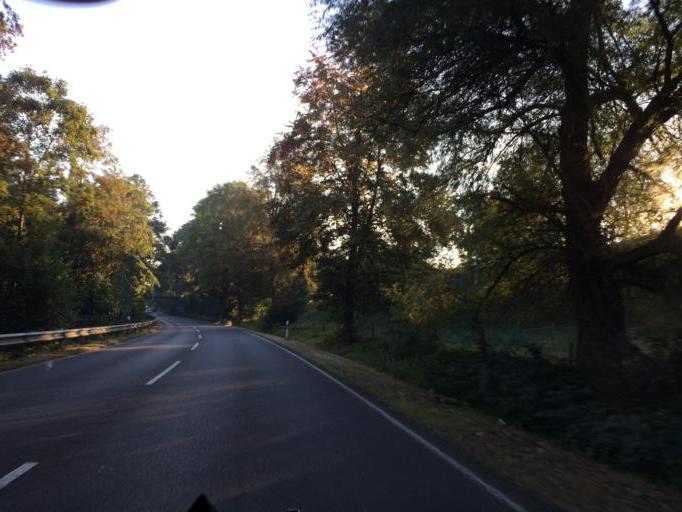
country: DE
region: North Rhine-Westphalia
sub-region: Regierungsbezirk Koln
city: Wachtberg
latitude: 50.6481
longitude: 7.1063
